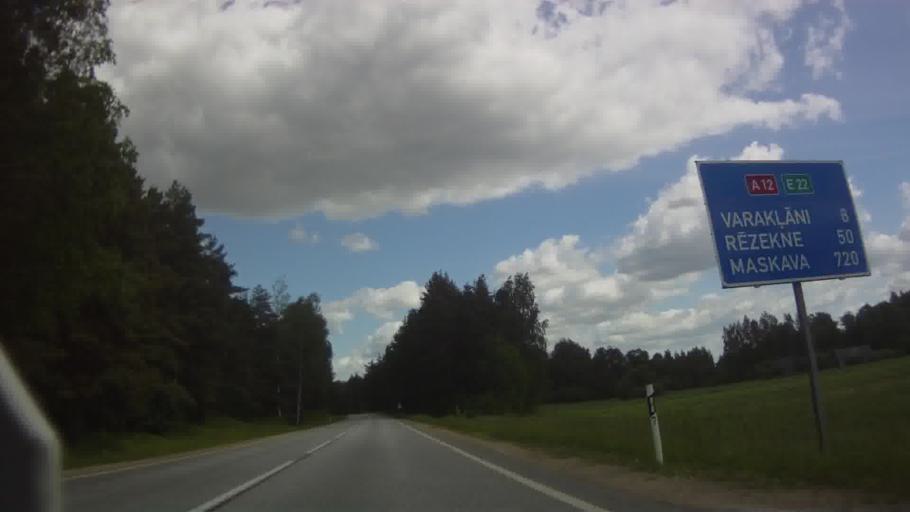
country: LV
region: Varaklani
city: Varaklani
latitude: 56.5687
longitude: 26.6451
